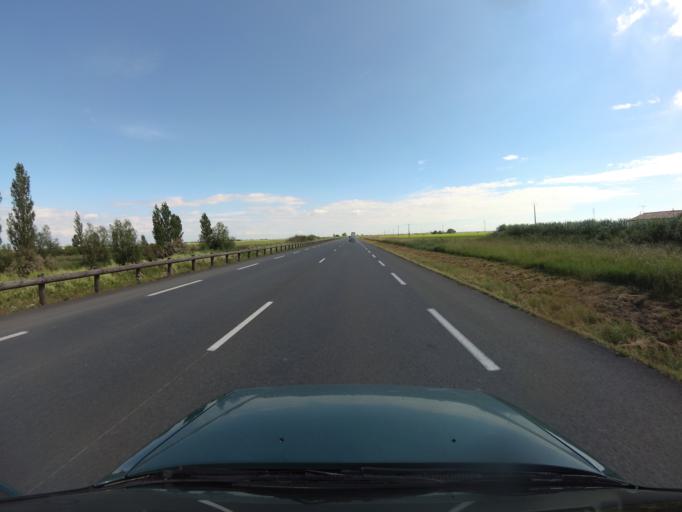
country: FR
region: Pays de la Loire
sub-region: Departement de la Vendee
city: Champagne-les-Marais
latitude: 46.3490
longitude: -1.0850
